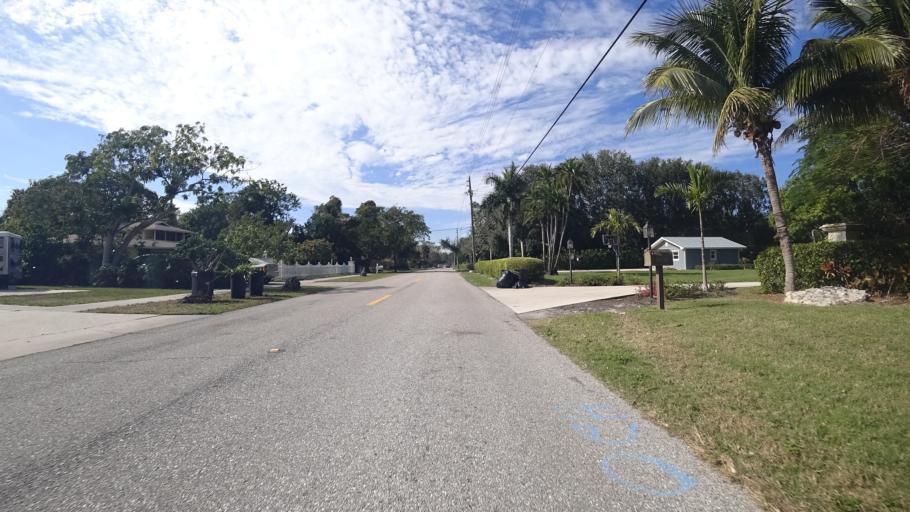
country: US
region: Florida
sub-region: Manatee County
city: West Bradenton
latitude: 27.5122
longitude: -82.6277
